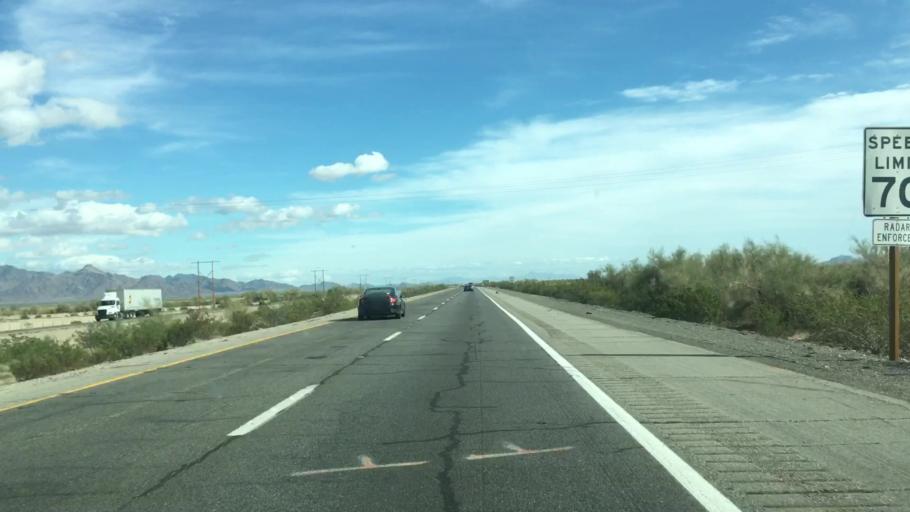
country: US
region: California
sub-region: Riverside County
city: Mesa Verde
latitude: 33.6059
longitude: -114.9794
